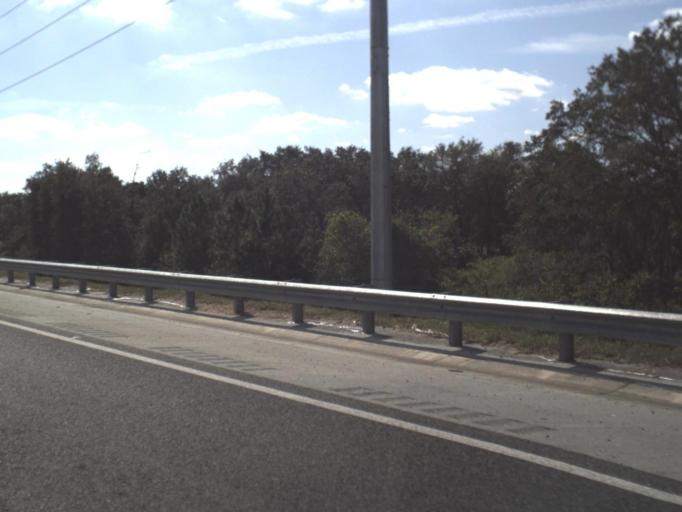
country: US
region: Florida
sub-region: Polk County
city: Citrus Ridge
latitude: 28.3373
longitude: -81.6158
